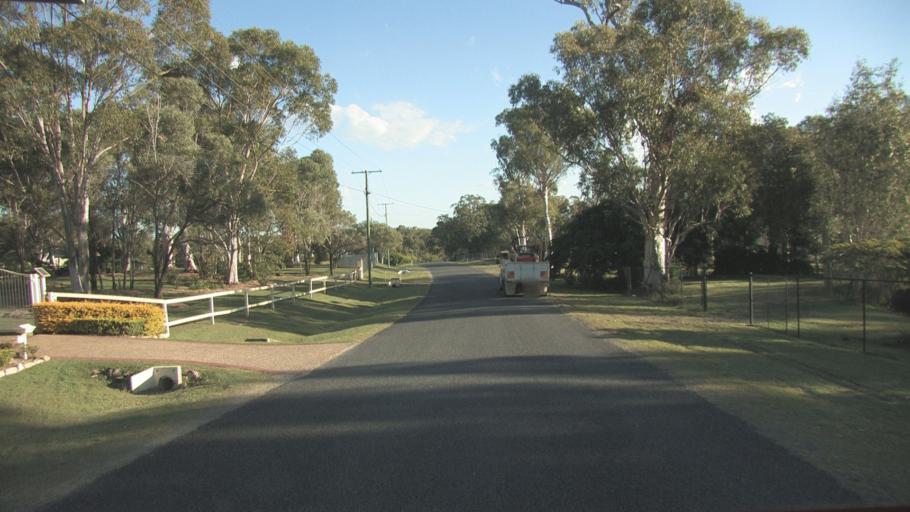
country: AU
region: Queensland
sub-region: Redland
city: Redland Bay
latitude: -27.6606
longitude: 153.2733
